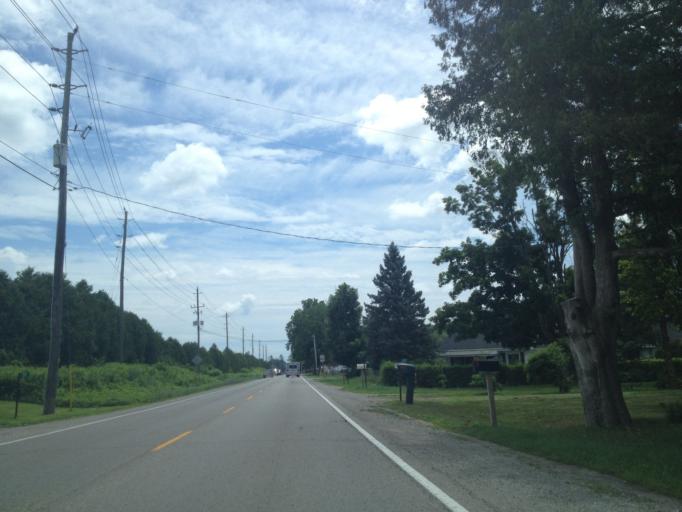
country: CA
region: Ontario
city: Norfolk County
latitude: 42.8369
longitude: -80.3417
